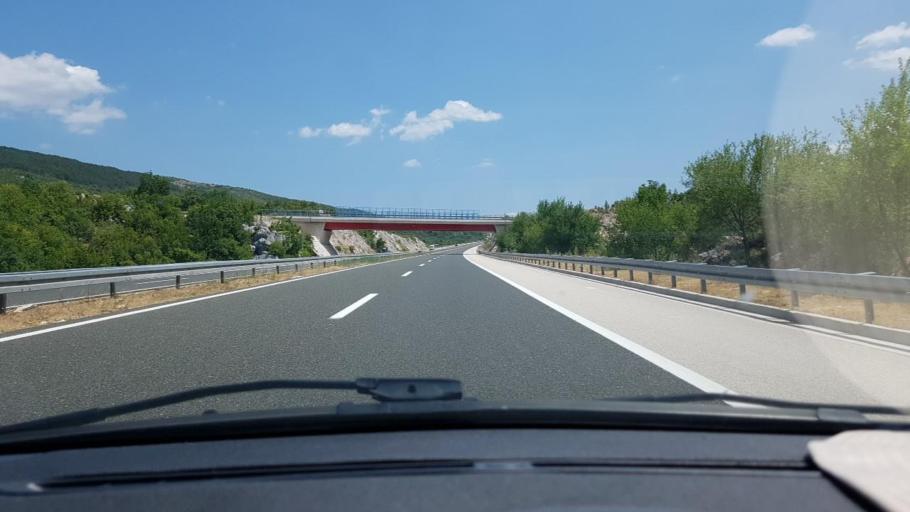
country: HR
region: Splitsko-Dalmatinska
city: Grubine
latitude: 43.3878
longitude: 17.0617
